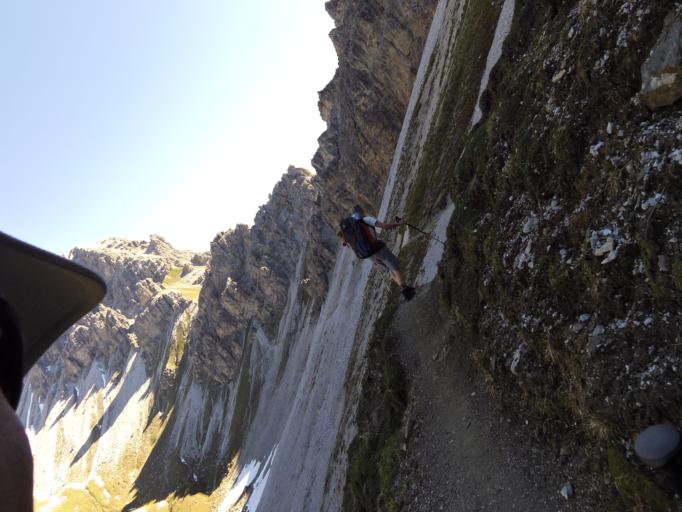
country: AT
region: Tyrol
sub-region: Politischer Bezirk Innsbruck Land
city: Neustift im Stubaital
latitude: 47.1334
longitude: 11.2748
